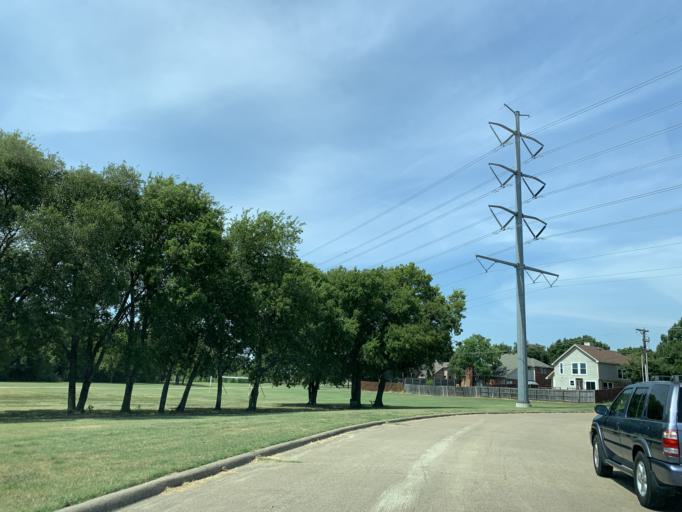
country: US
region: Texas
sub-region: Dallas County
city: Grand Prairie
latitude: 32.6623
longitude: -97.0383
